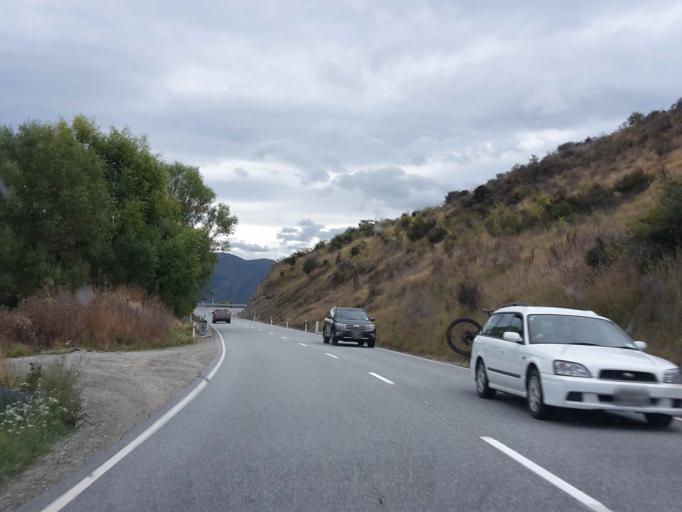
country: NZ
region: Otago
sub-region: Queenstown-Lakes District
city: Arrowtown
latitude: -44.9878
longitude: 168.9046
